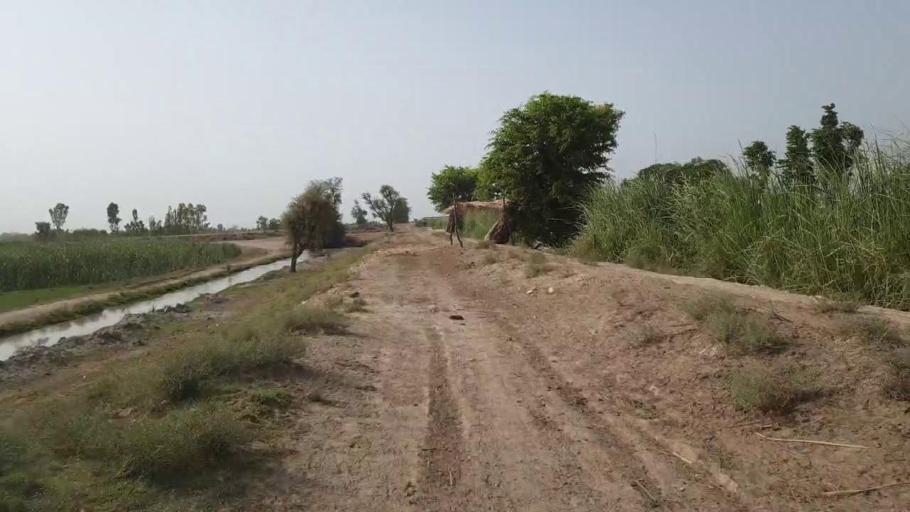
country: PK
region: Sindh
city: Daur
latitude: 26.4553
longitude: 68.1584
